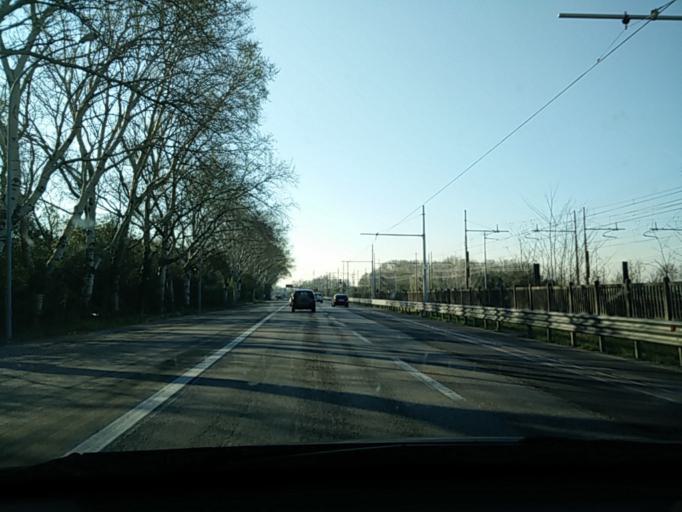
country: IT
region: Veneto
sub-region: Provincia di Venezia
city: Campalto
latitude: 45.4653
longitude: 12.2780
